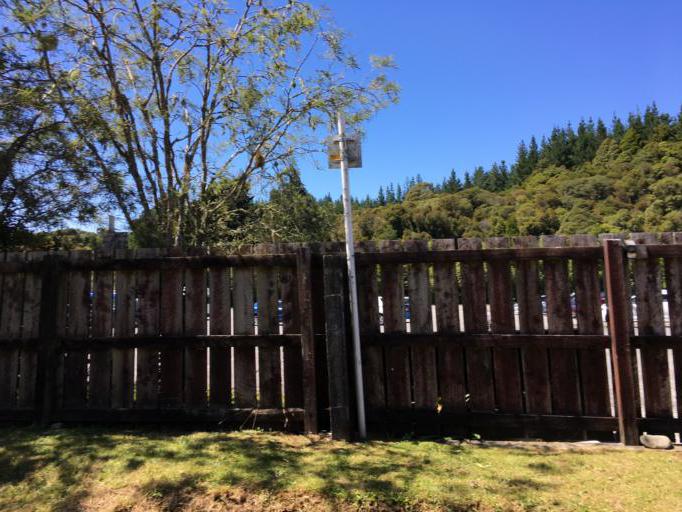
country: NZ
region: West Coast
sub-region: Grey District
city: Greymouth
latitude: -42.5351
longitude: 171.1819
